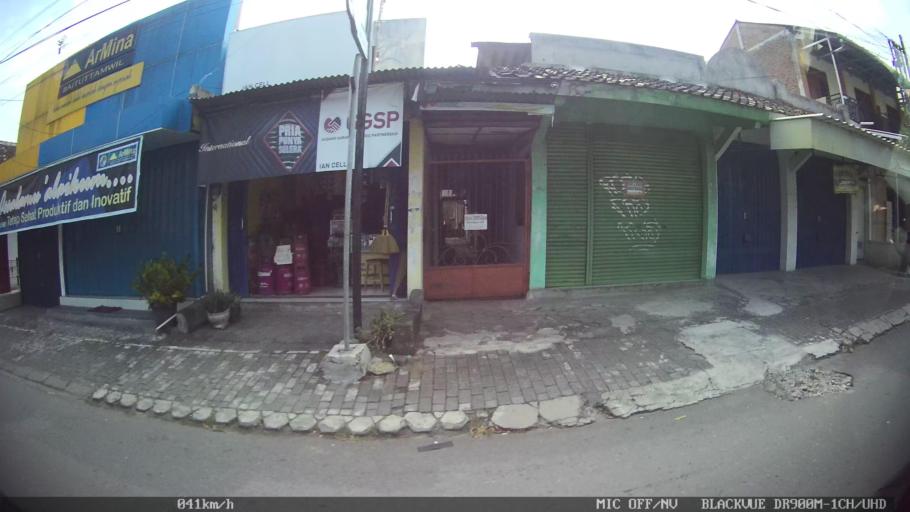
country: ID
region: Daerah Istimewa Yogyakarta
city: Depok
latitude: -7.7628
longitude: 110.4322
